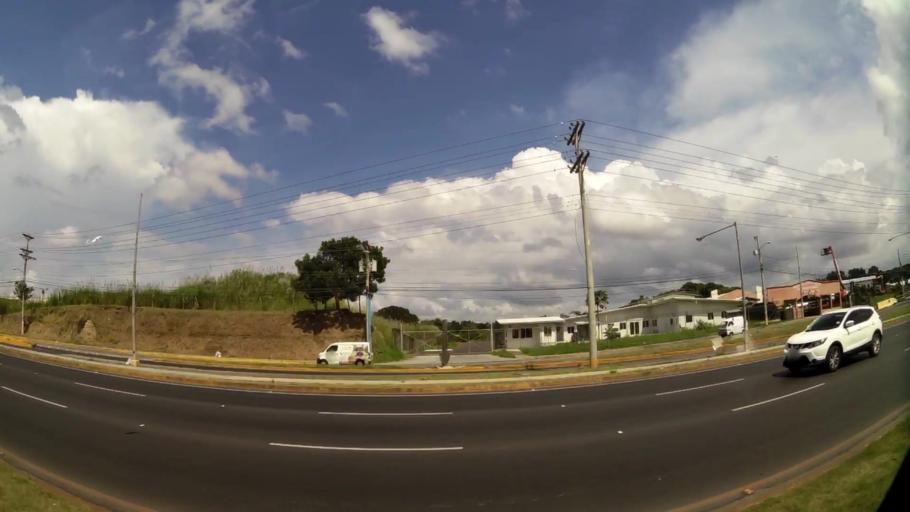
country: PA
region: Panama
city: San Miguelito
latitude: 9.0495
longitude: -79.4578
